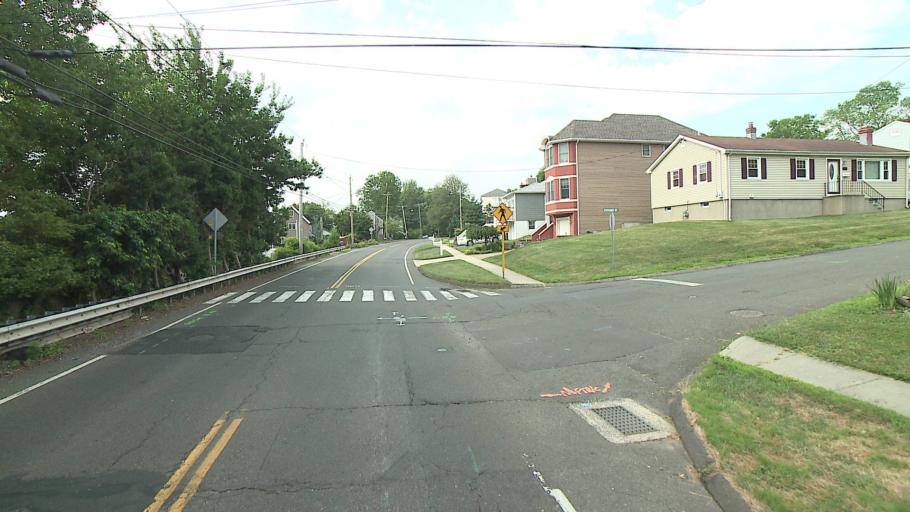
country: US
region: Connecticut
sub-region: New Haven County
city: Woodmont
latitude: 41.2164
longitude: -73.0077
